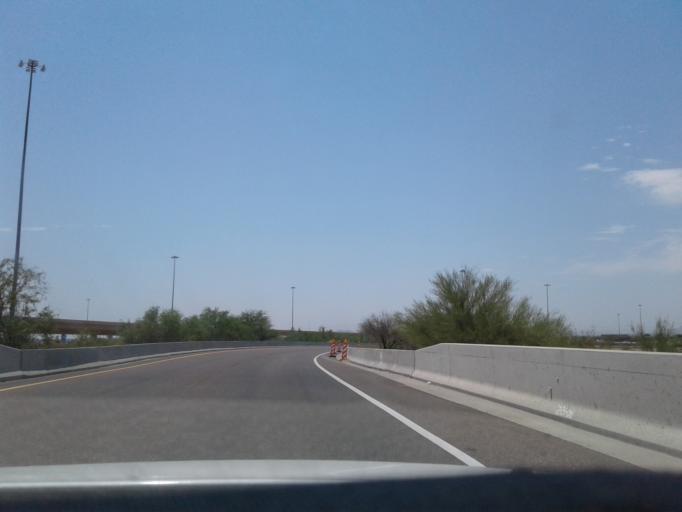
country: US
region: Arizona
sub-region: Maricopa County
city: Guadalupe
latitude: 33.2997
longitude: -111.9735
